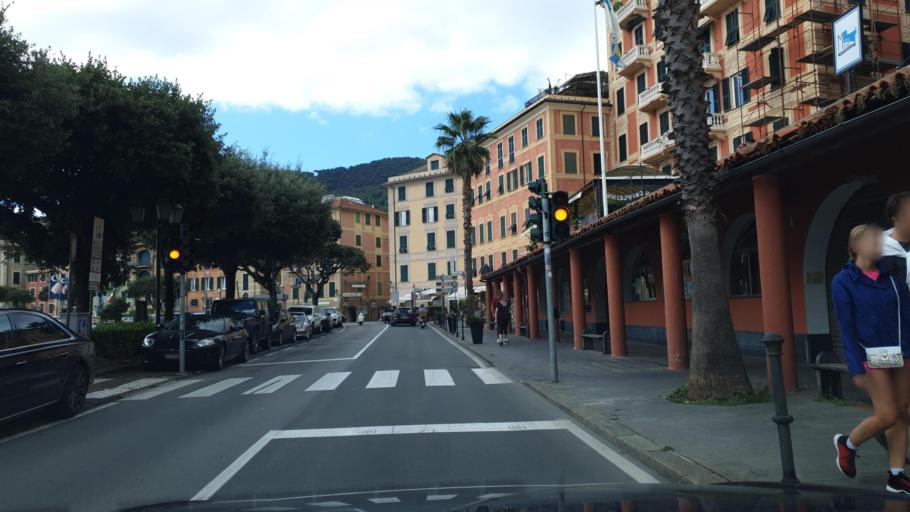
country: IT
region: Liguria
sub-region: Provincia di Genova
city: Santa Margherita Ligure
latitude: 44.3315
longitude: 9.2132
